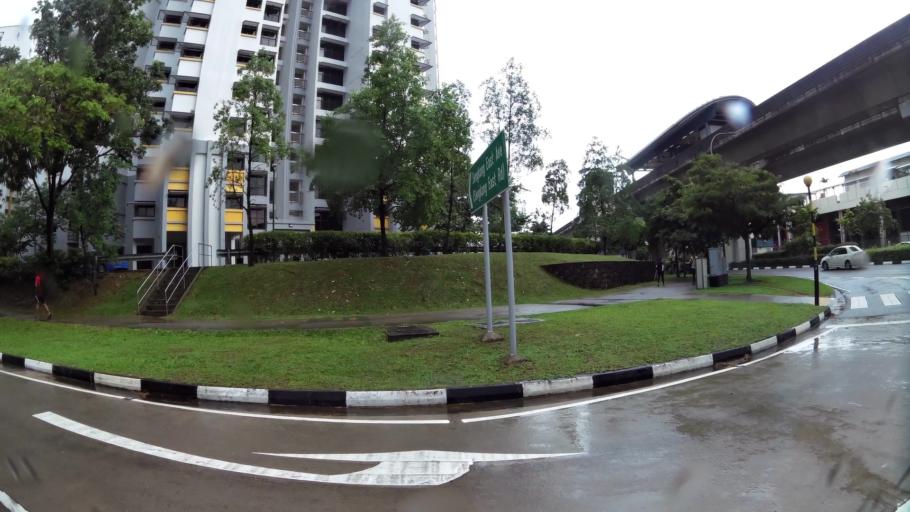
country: MY
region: Johor
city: Kampung Pasir Gudang Baru
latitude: 1.3898
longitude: 103.8856
